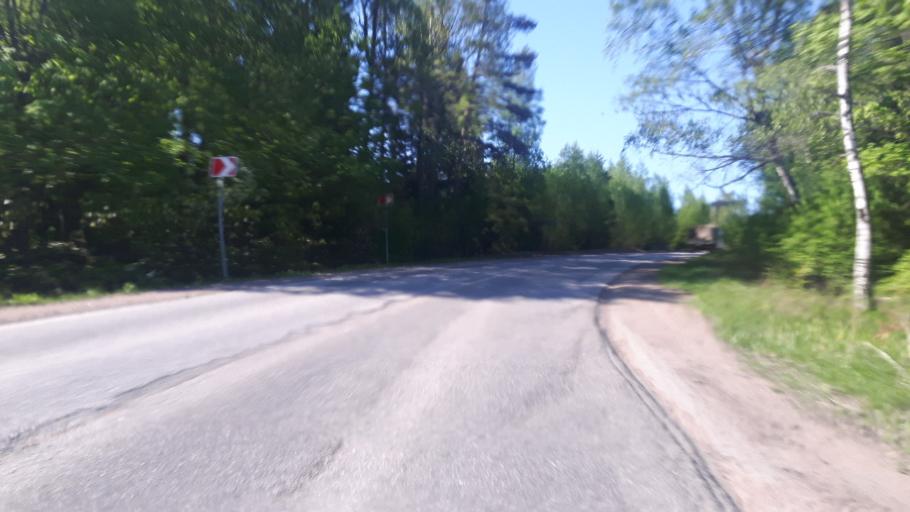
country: RU
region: Leningrad
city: Vyborg
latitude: 60.6476
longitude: 28.7492
